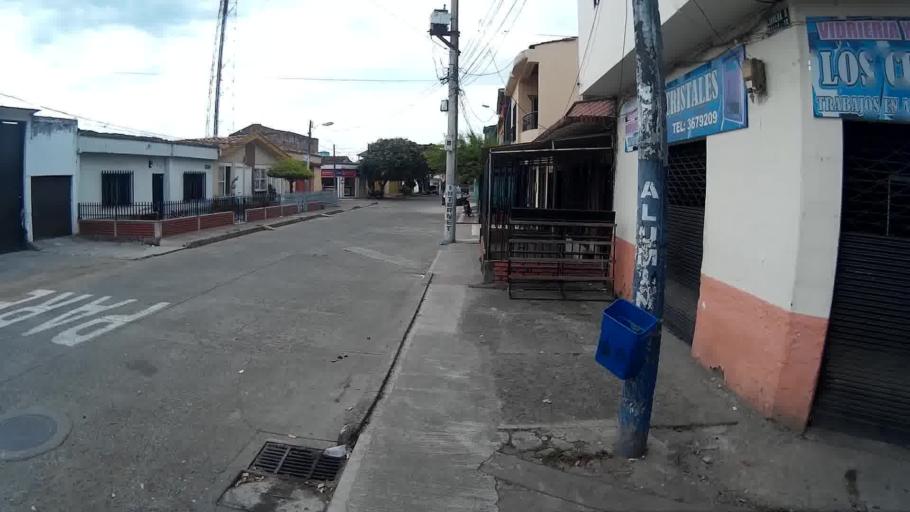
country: CO
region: Risaralda
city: La Virginia
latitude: 4.8973
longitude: -75.8825
